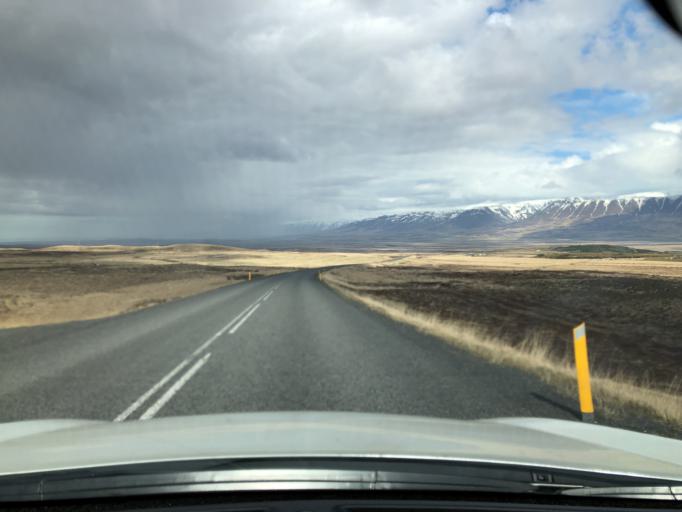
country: IS
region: Northwest
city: Saudarkrokur
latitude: 65.5341
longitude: -19.5116
